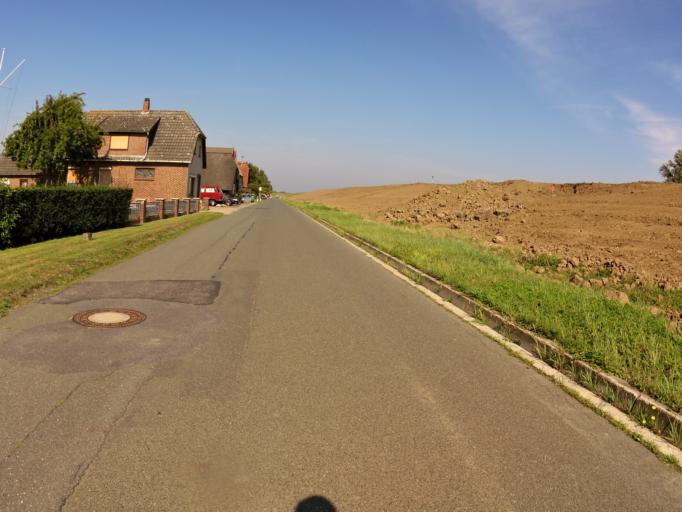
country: DE
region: Lower Saxony
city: Neuenkirchen
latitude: 53.2009
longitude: 8.4963
